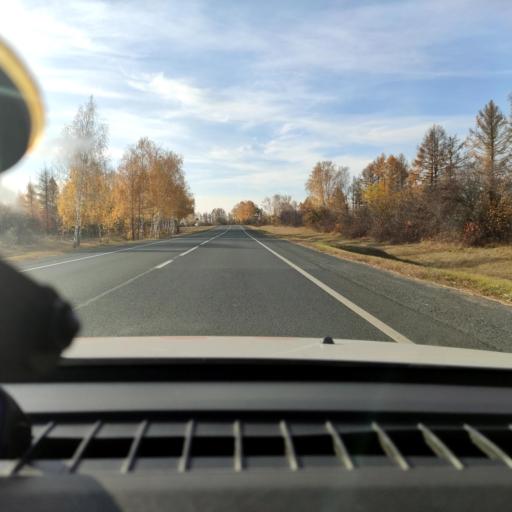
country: RU
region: Samara
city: Bereza
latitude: 53.4801
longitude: 50.1167
